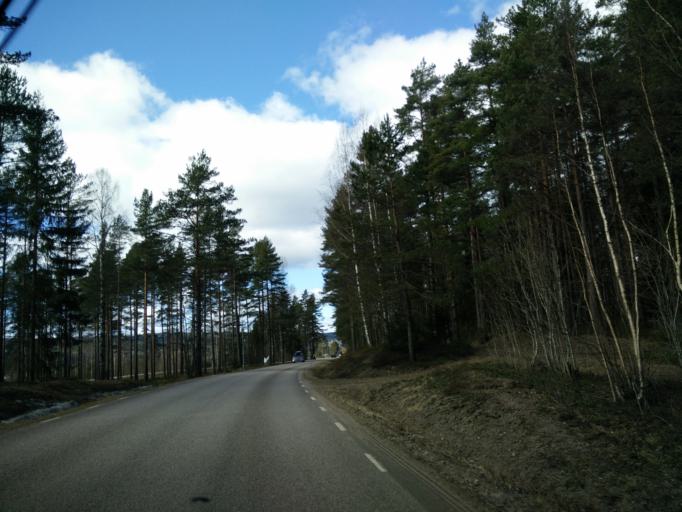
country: SE
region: Vaermland
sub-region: Hagfors Kommun
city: Hagfors
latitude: 59.8863
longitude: 13.7170
